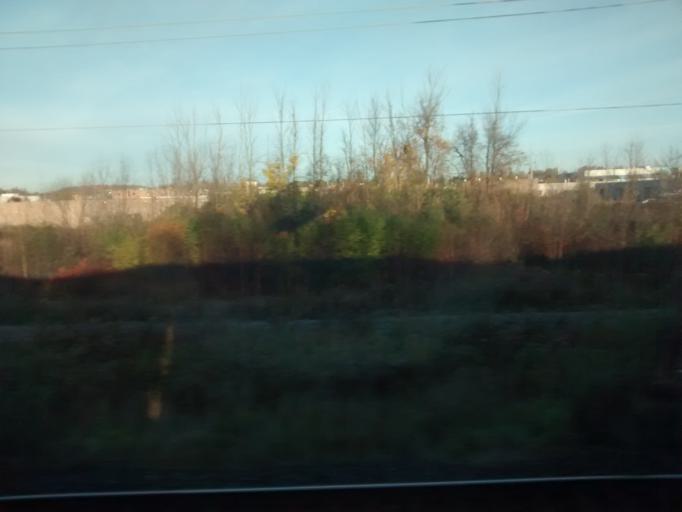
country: CA
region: Ontario
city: Oakville
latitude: 43.4103
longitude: -79.7290
